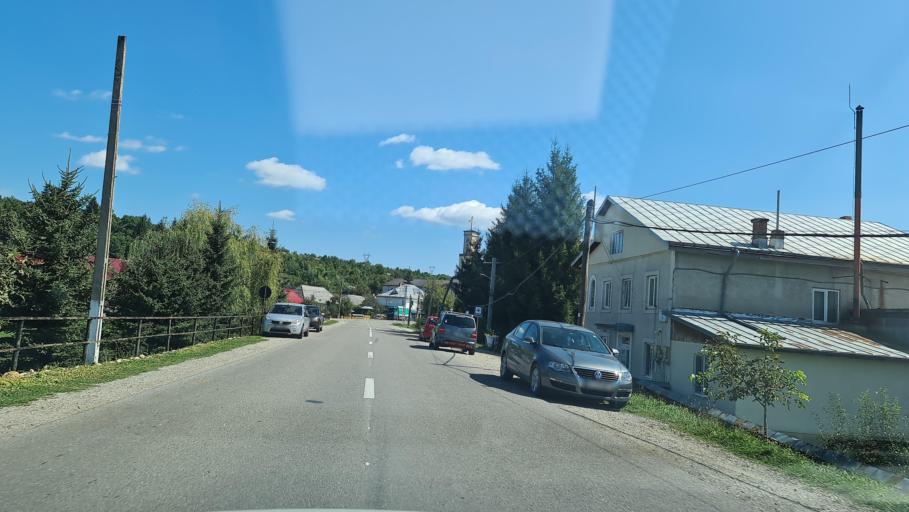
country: RO
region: Bacau
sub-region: Comuna Balcani
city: Frumoasa
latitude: 46.6637
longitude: 26.5374
